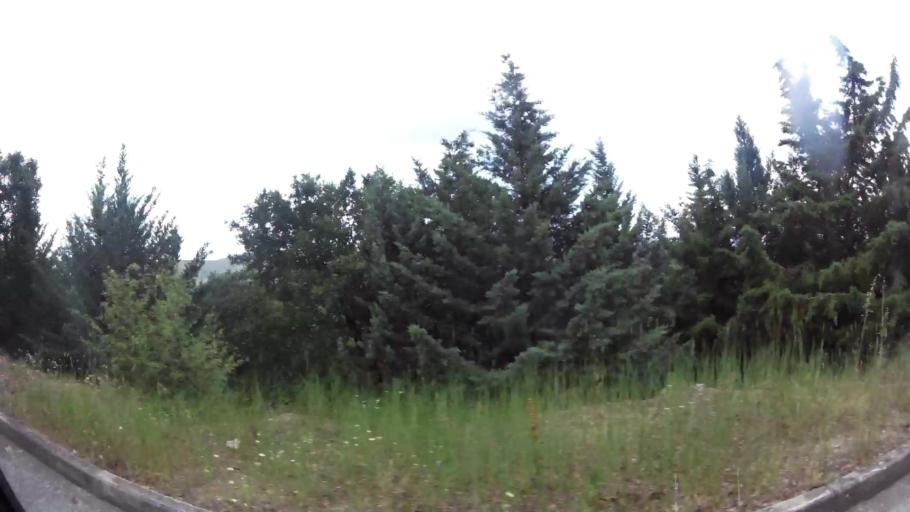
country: GR
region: West Macedonia
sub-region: Nomos Kozanis
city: Koila
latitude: 40.3244
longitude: 21.8243
